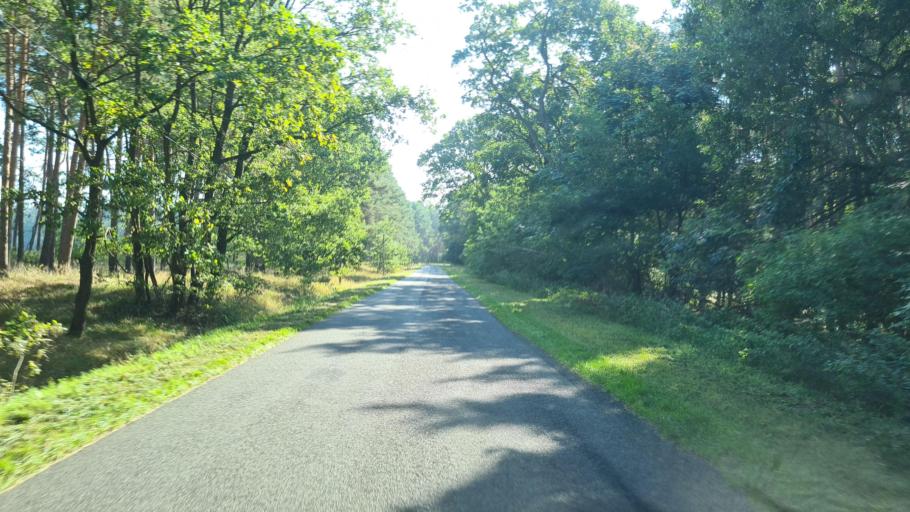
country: DE
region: Brandenburg
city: Friesack
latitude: 52.7788
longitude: 12.6181
